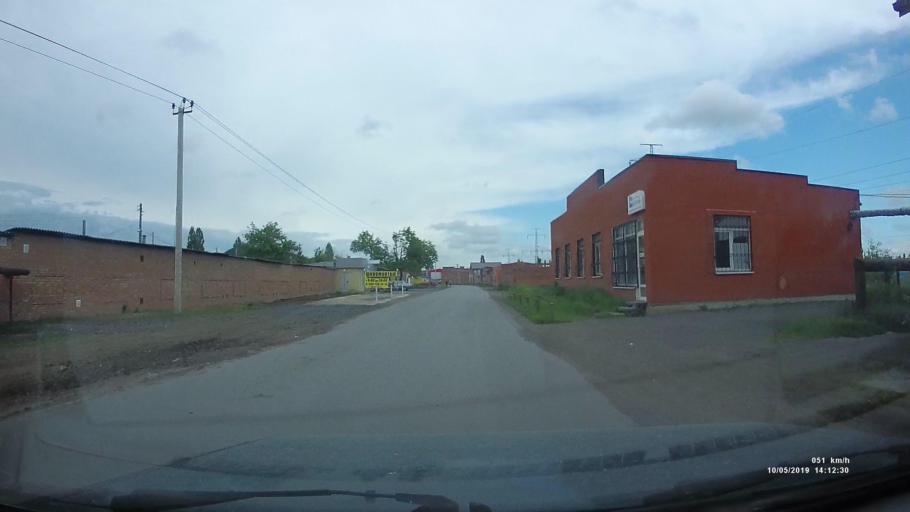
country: RU
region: Rostov
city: Azov
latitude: 47.0926
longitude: 39.4263
